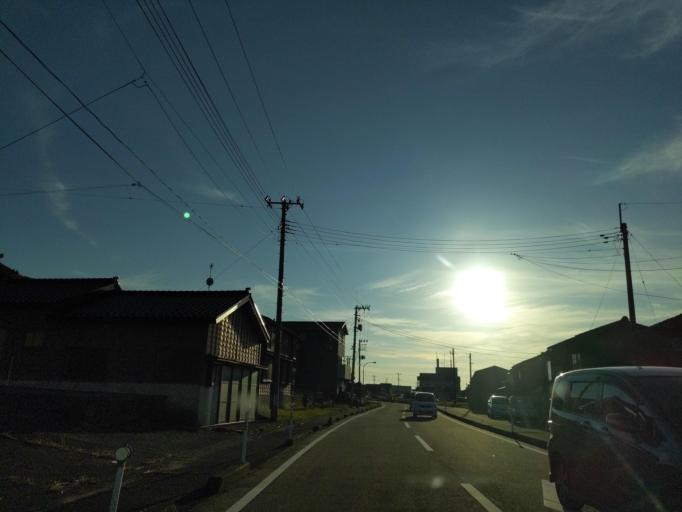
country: JP
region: Niigata
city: Nagaoka
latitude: 37.5411
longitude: 138.6844
